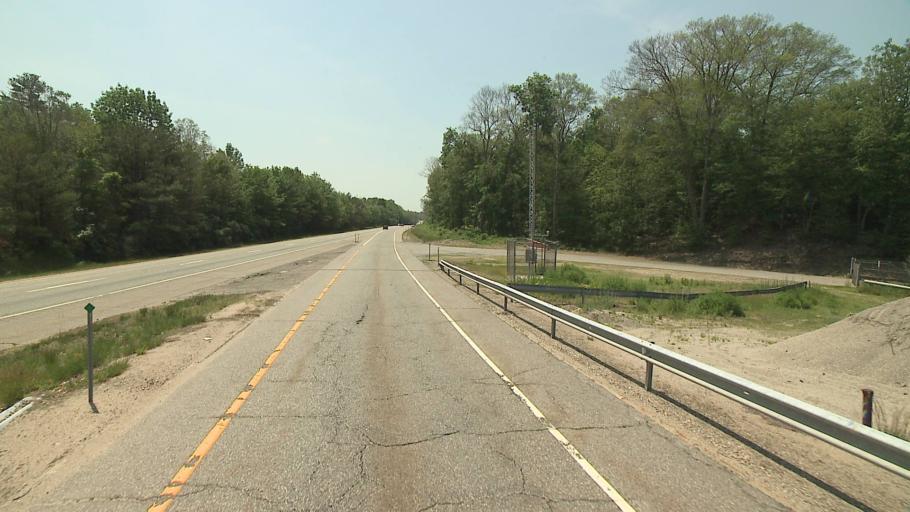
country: US
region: Connecticut
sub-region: Windham County
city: Thompson
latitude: 41.9645
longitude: -71.8740
